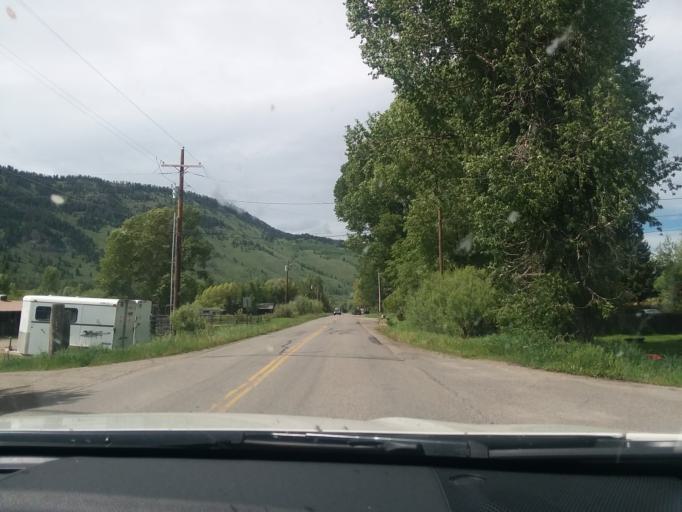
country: US
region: Wyoming
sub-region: Teton County
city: Wilson
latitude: 43.5009
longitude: -110.8718
